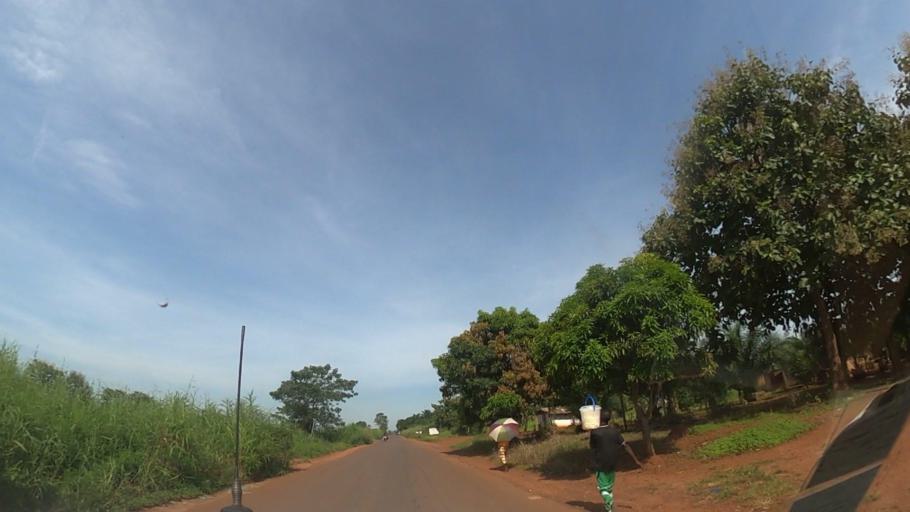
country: CF
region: Ombella-Mpoko
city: Bimbo
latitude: 4.3133
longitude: 18.4738
